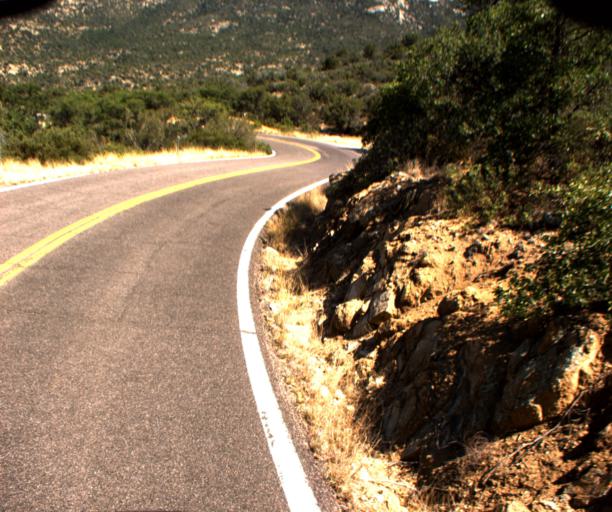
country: US
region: Arizona
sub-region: Graham County
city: Swift Trail Junction
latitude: 32.6663
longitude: -109.8000
